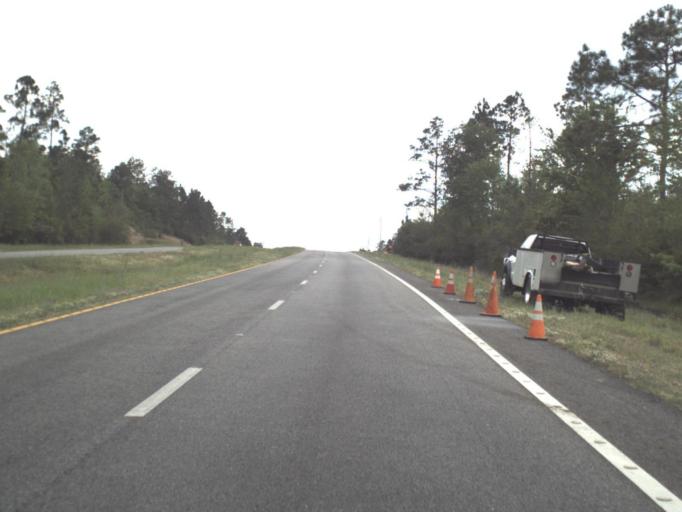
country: US
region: Florida
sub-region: Escambia County
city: Molino
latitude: 30.7700
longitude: -87.3404
